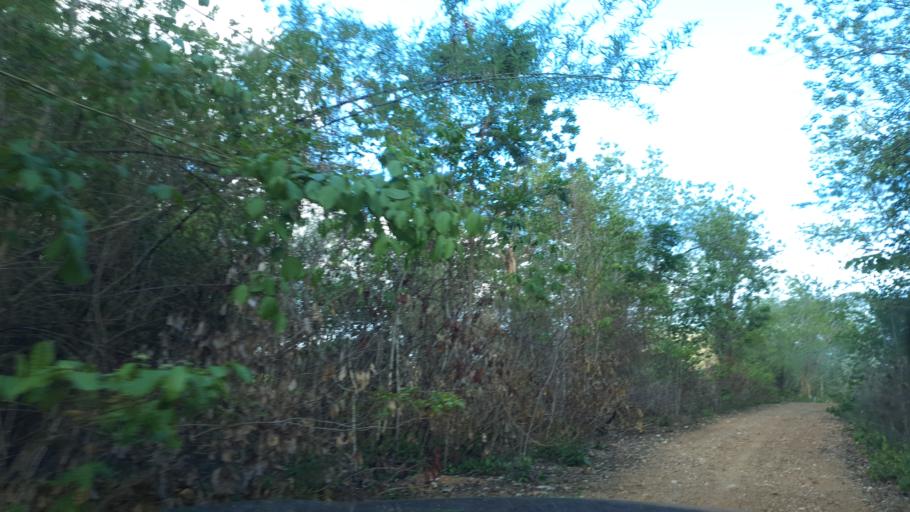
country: TH
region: Lampang
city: Sop Prap
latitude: 17.8506
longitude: 99.2844
